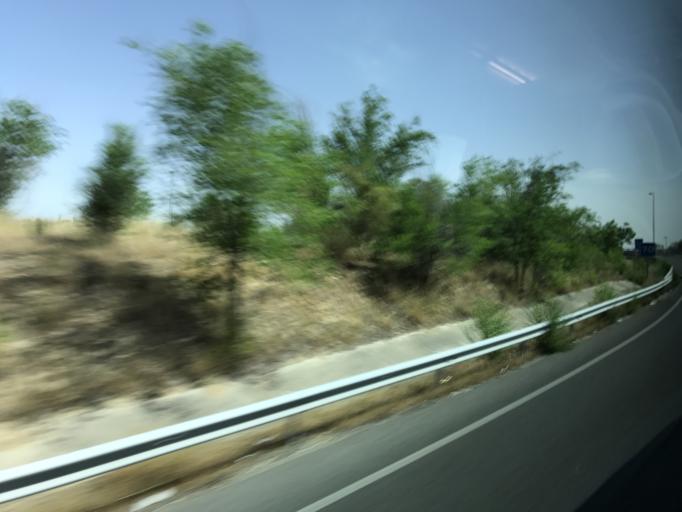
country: ES
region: Madrid
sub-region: Provincia de Madrid
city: Vicalvaro
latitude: 40.4124
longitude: -3.6188
